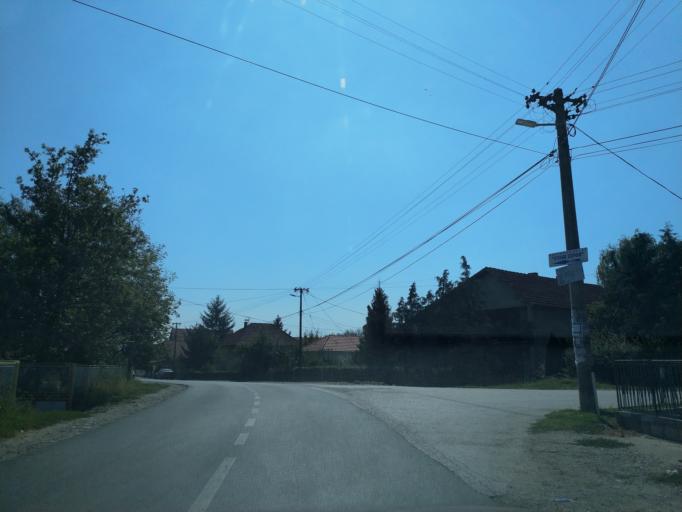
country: RS
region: Central Serbia
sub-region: Rasinski Okrug
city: Krusevac
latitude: 43.6147
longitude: 21.2964
